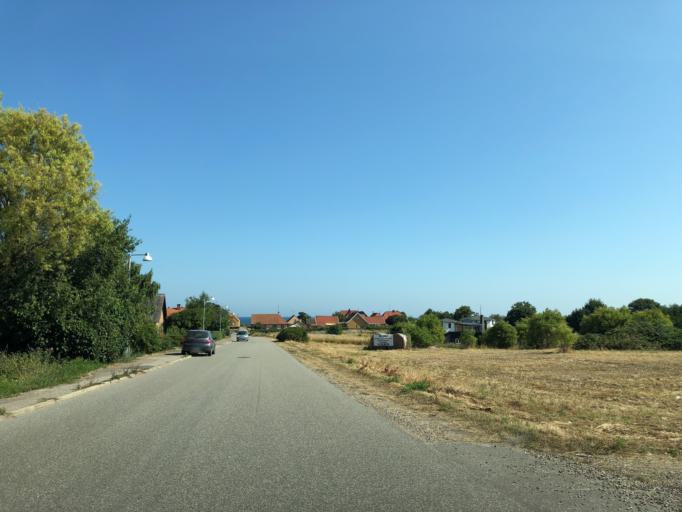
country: DK
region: Zealand
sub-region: Odsherred Kommune
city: Asnaes
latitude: 55.9711
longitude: 11.3590
